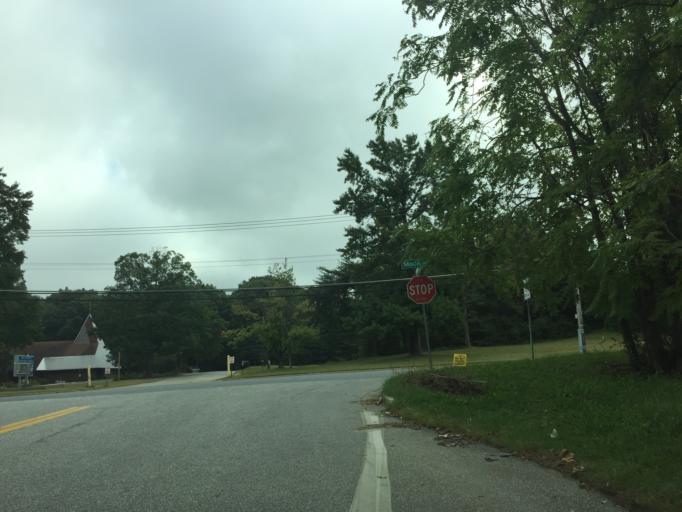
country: US
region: Maryland
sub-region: Baltimore County
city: Rossville
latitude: 39.3268
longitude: -76.4710
